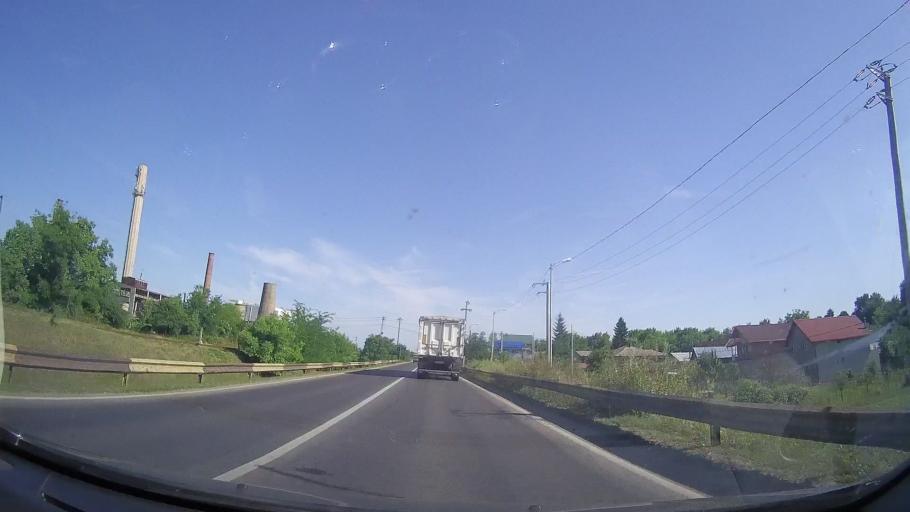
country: RO
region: Prahova
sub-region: Comuna Blejoiu
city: Blejoi
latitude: 44.9923
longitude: 26.0131
